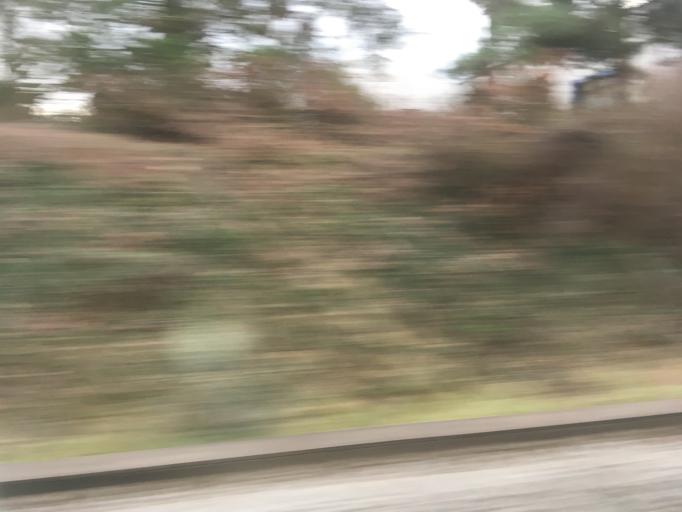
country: GB
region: England
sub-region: Royal Borough of Windsor and Maidenhead
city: White Waltham
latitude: 51.5048
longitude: -0.7718
